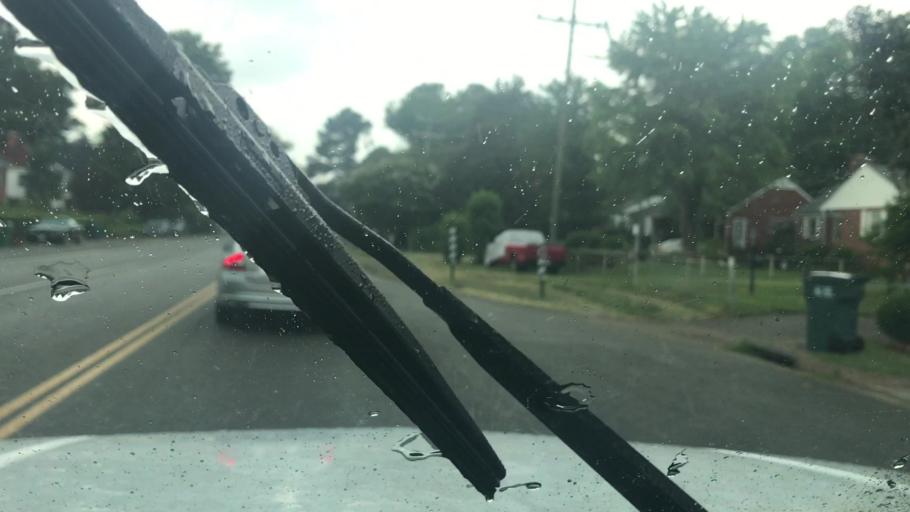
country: US
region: Virginia
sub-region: Henrico County
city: Tuckahoe
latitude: 37.5946
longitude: -77.5325
